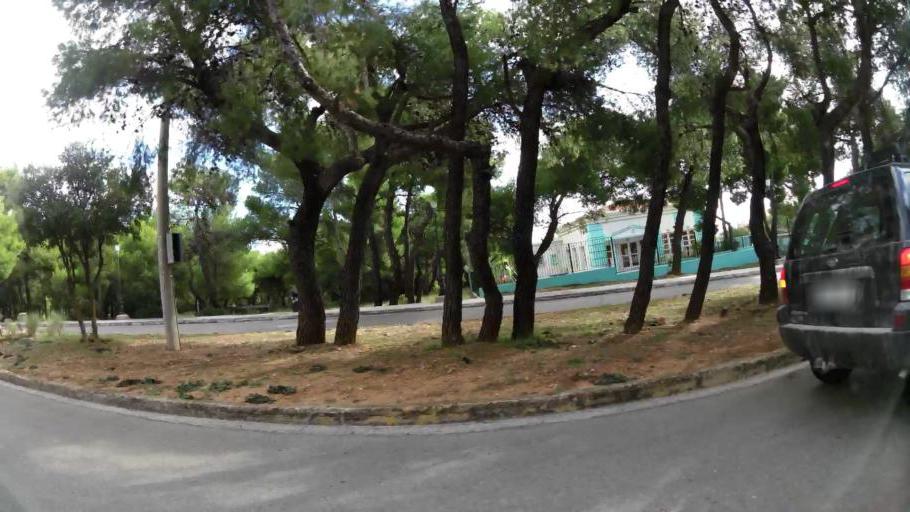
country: GR
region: Attica
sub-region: Nomarchia Anatolikis Attikis
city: Thrakomakedones
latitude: 38.1339
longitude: 23.7566
